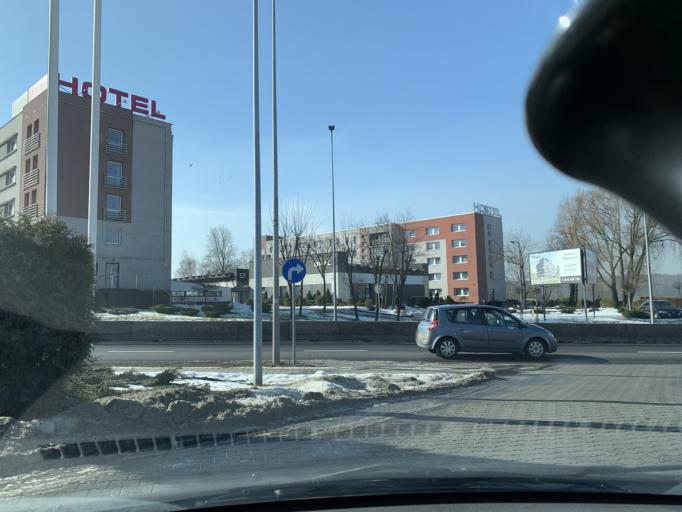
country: PL
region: Silesian Voivodeship
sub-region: Powiat tarnogorski
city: Radzionkow
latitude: 50.3720
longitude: 18.8940
